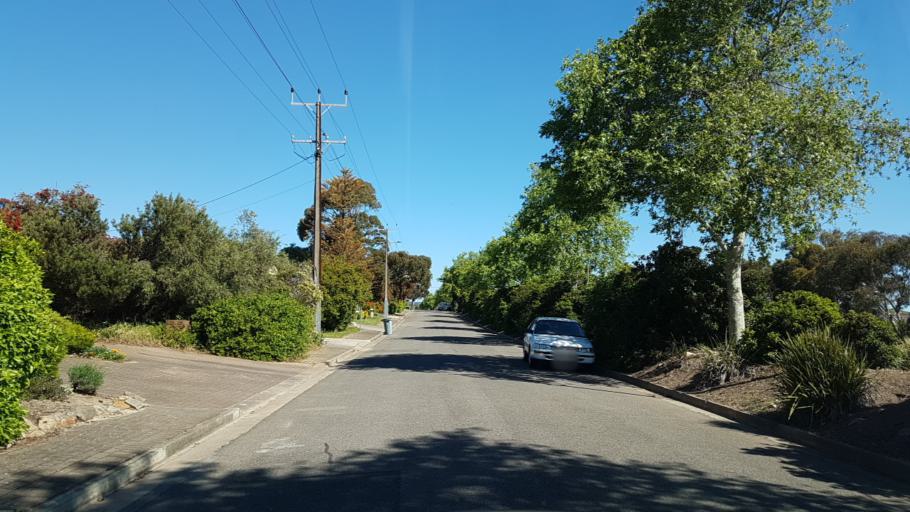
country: AU
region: South Australia
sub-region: Onkaparinga
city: Bedford Park
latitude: -35.0434
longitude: 138.5704
